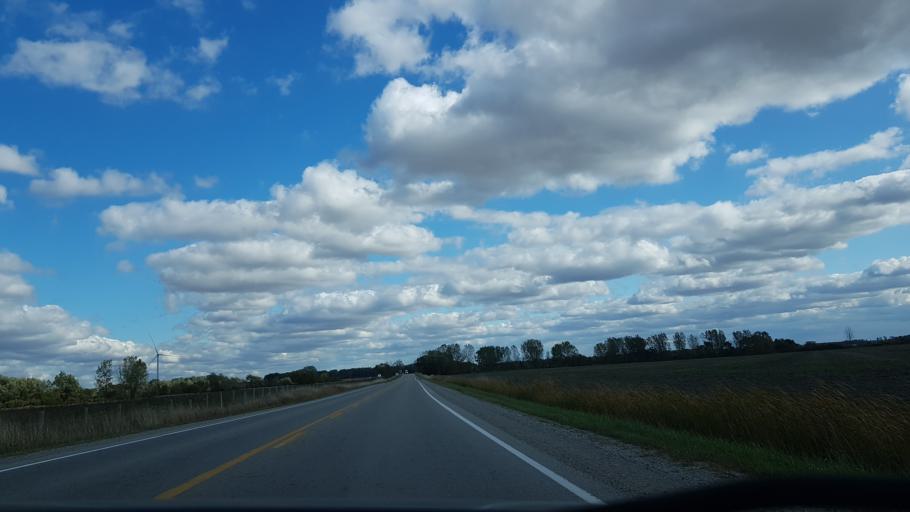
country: CA
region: Ontario
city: Lambton Shores
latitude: 43.2394
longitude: -81.7807
